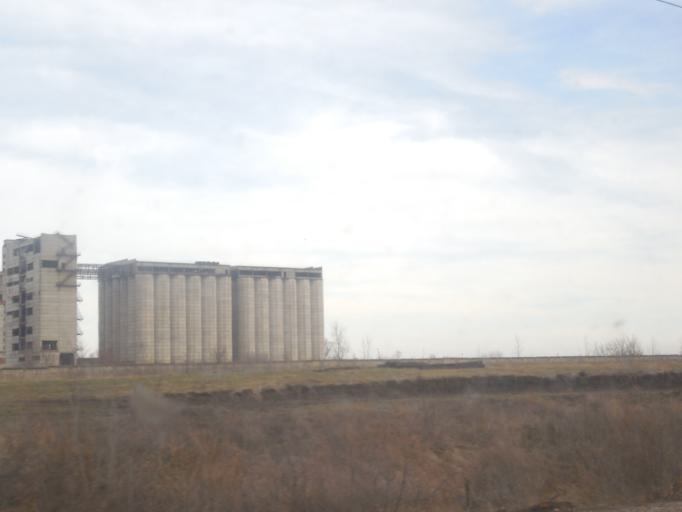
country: RU
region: Adygeya
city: Adygeysk
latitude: 44.8307
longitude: 39.1939
